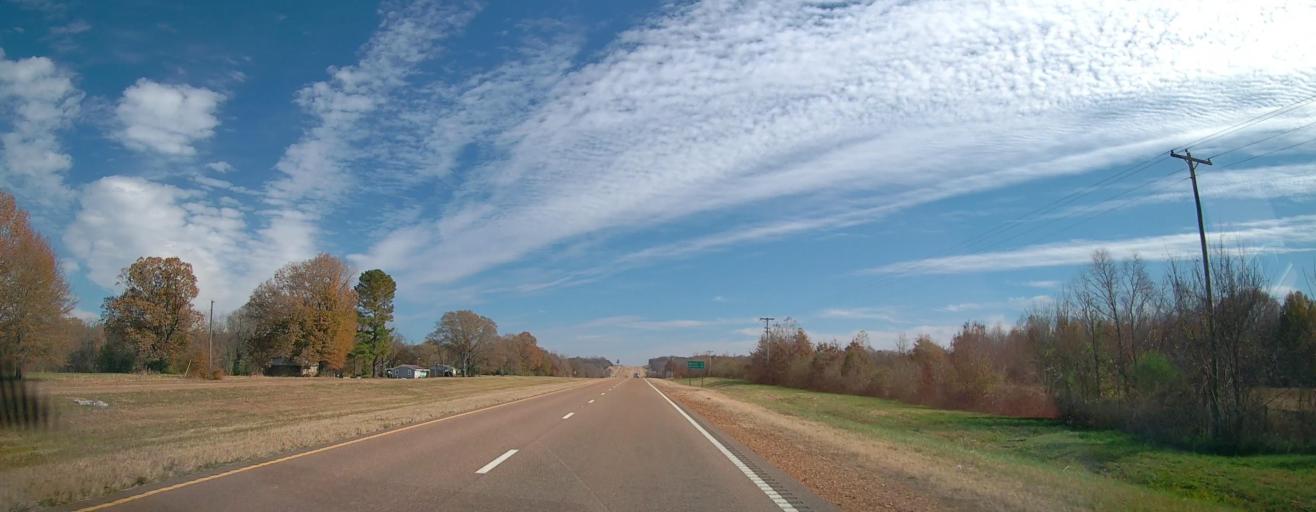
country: US
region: Mississippi
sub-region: Benton County
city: Ashland
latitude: 34.9461
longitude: -89.2085
